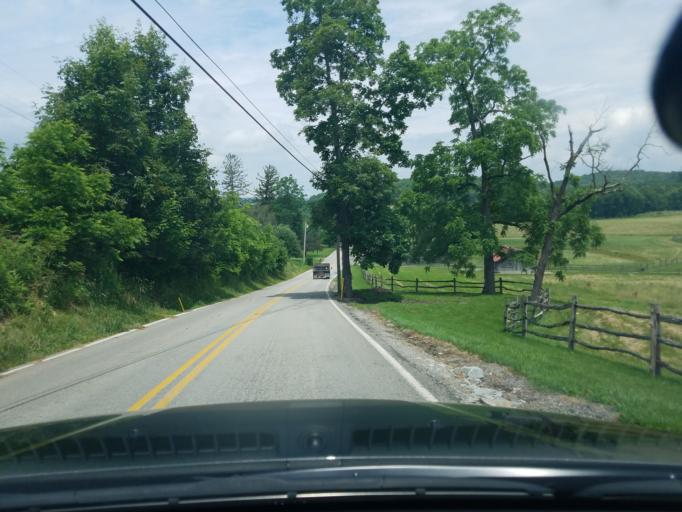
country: US
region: Pennsylvania
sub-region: Fayette County
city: Bear Rocks
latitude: 40.1564
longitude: -79.3439
